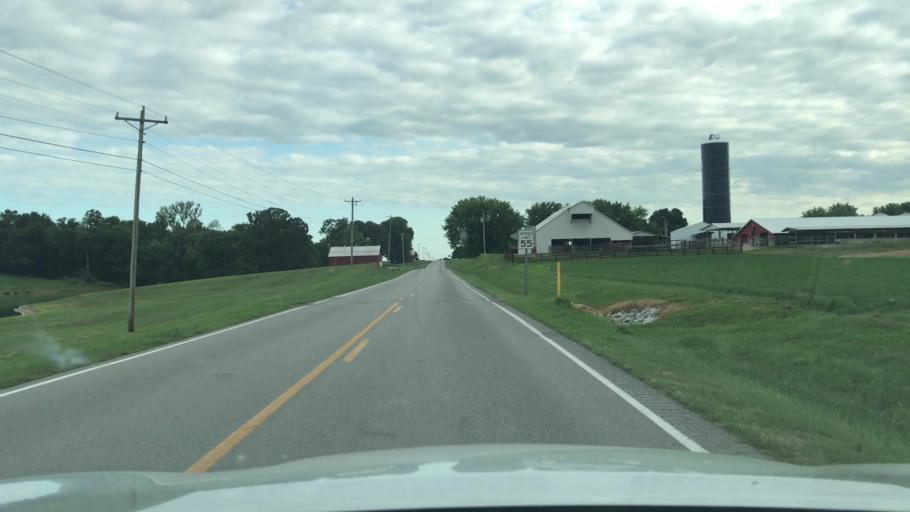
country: US
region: Kentucky
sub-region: Todd County
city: Elkton
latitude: 36.7585
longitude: -87.1674
